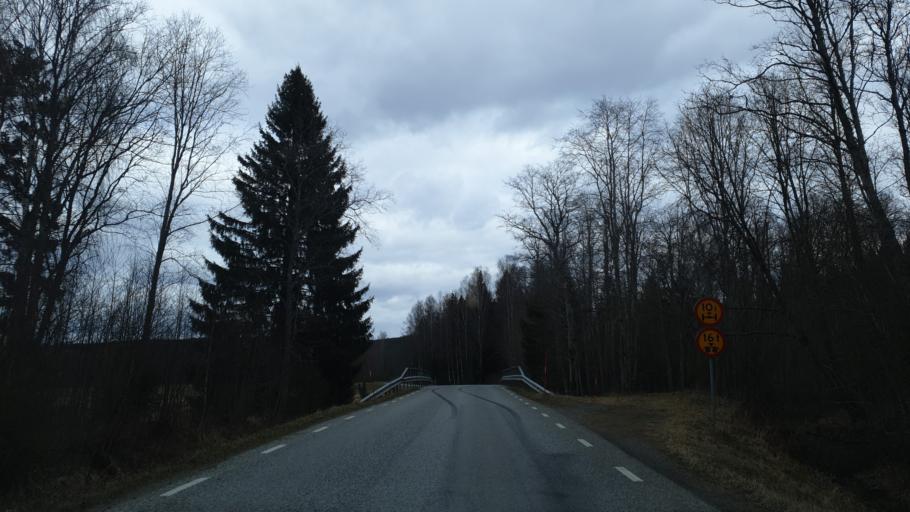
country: SE
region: OErebro
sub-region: Nora Kommun
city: As
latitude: 59.6294
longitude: 14.9371
